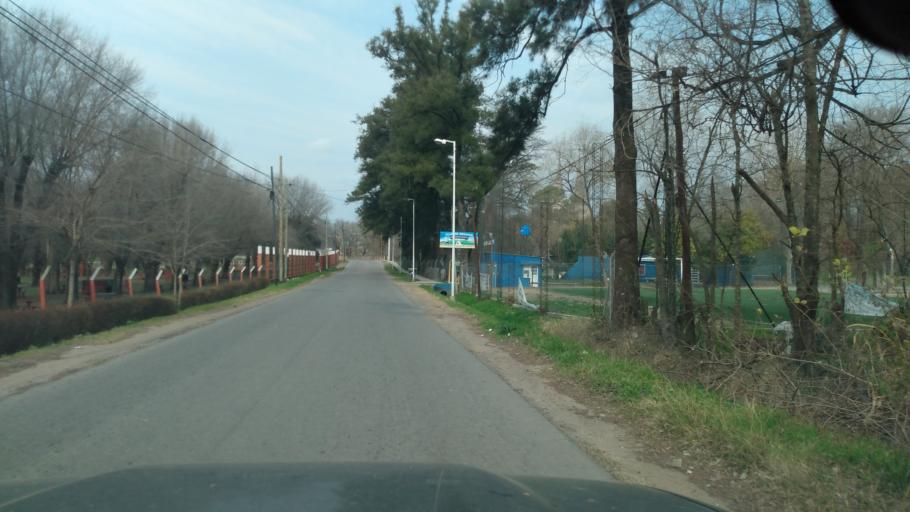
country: AR
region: Buenos Aires
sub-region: Partido de Lujan
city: Lujan
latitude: -34.5582
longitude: -59.1234
